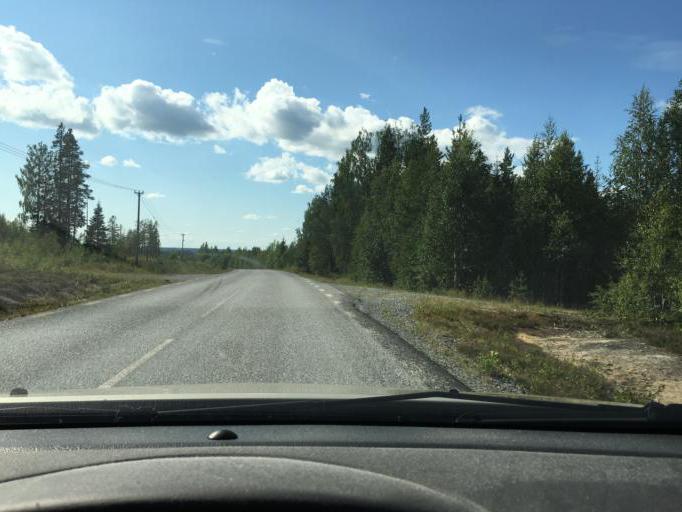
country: SE
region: Norrbotten
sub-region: Kalix Kommun
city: Toere
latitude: 66.0633
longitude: 22.6208
